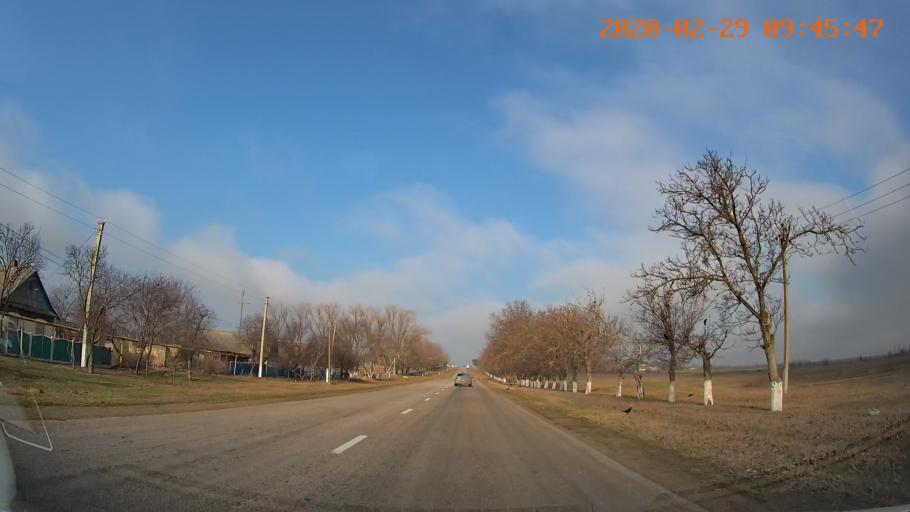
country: MD
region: Telenesti
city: Crasnoe
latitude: 46.6618
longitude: 29.8063
